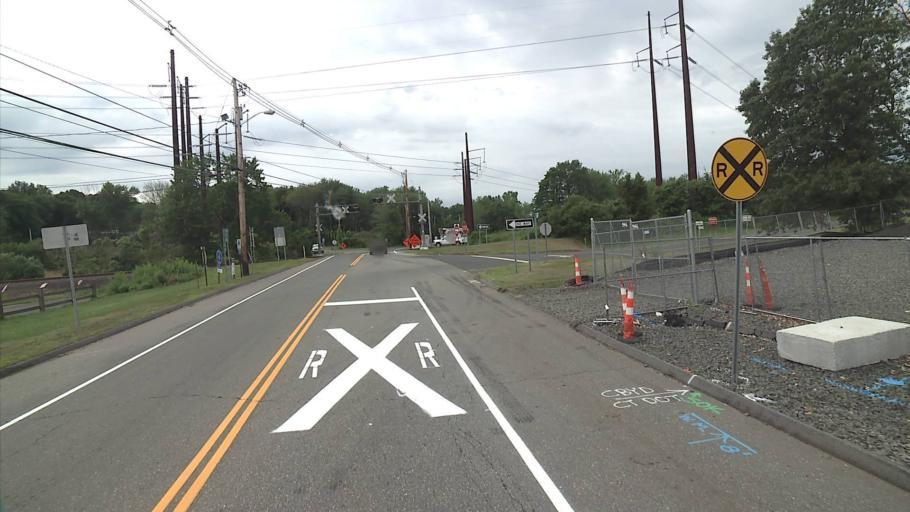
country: US
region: Connecticut
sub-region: New Haven County
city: Wallingford Center
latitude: 41.4335
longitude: -72.8026
